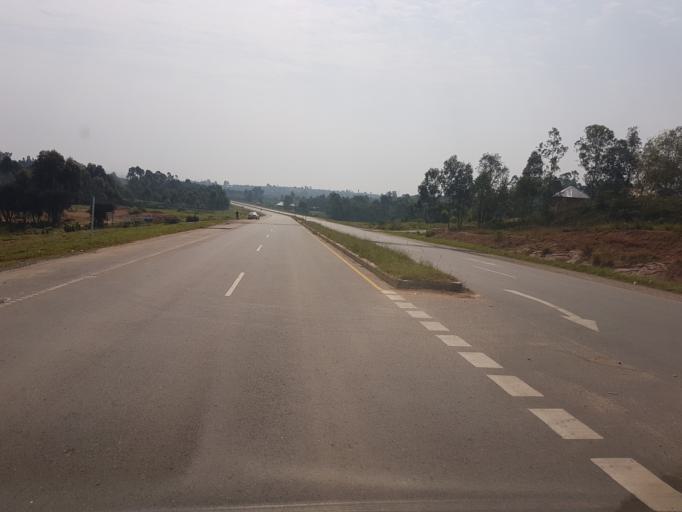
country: UG
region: Western Region
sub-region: Mbarara District
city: Bwizibwera
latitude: -0.6384
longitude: 30.5935
